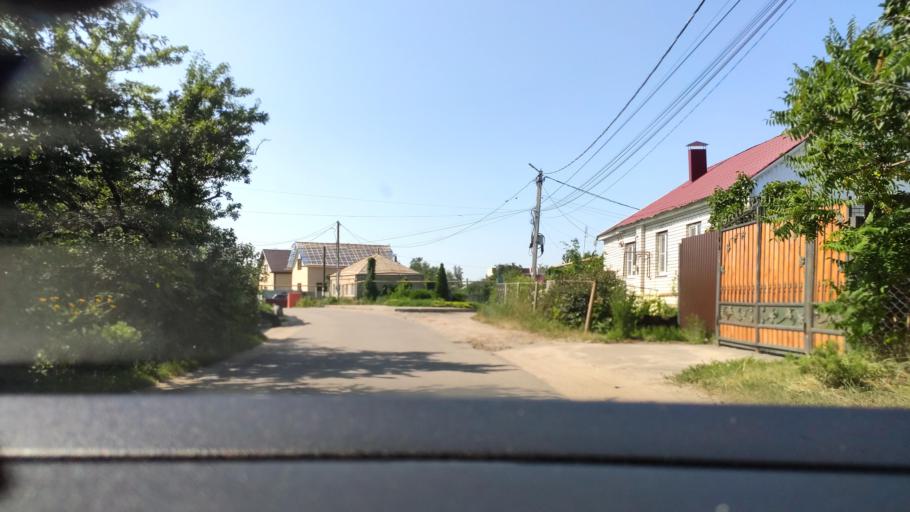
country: RU
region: Voronezj
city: Novaya Usman'
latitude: 51.6382
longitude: 39.4121
